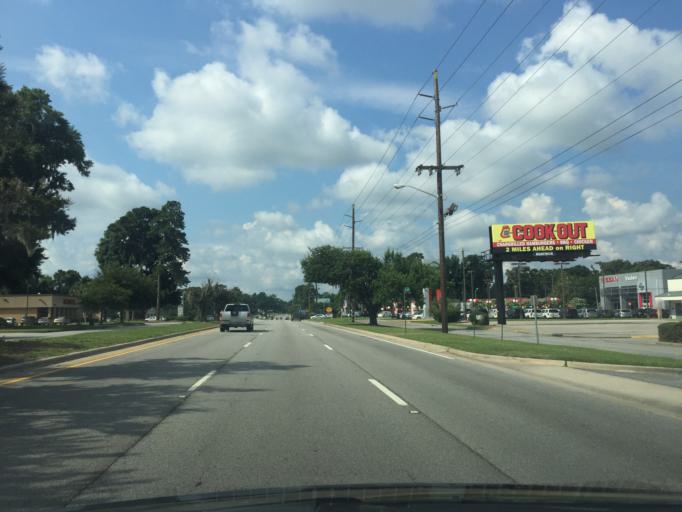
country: US
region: Georgia
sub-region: Chatham County
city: Montgomery
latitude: 31.9876
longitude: -81.1315
